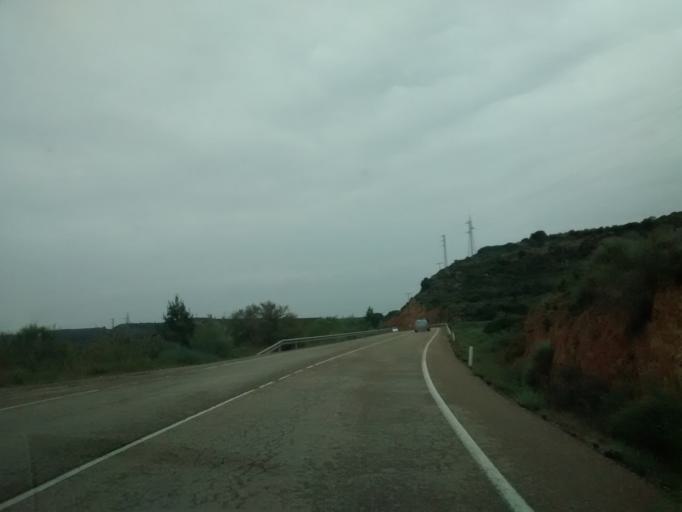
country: ES
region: Aragon
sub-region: Provincia de Zaragoza
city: Caspe
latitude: 41.2575
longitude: -0.0671
